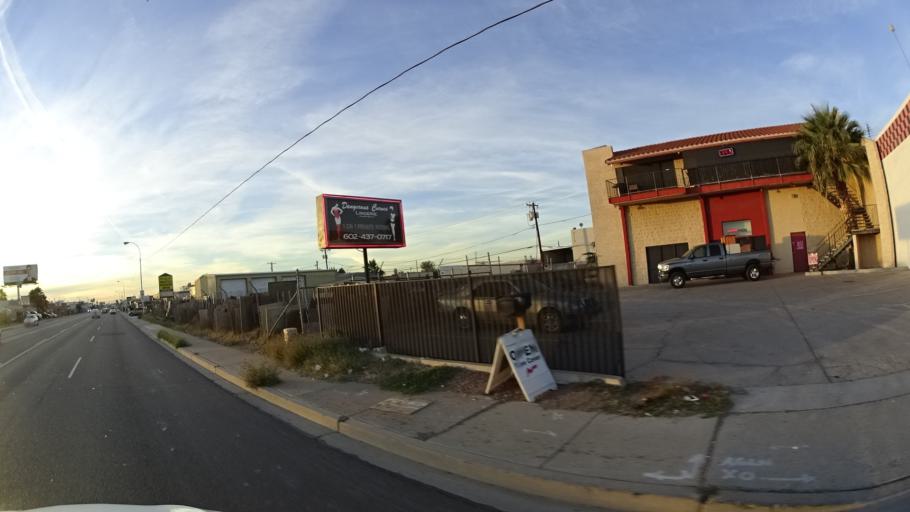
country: US
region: Arizona
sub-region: Maricopa County
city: Tempe Junction
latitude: 33.4219
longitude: -111.9874
